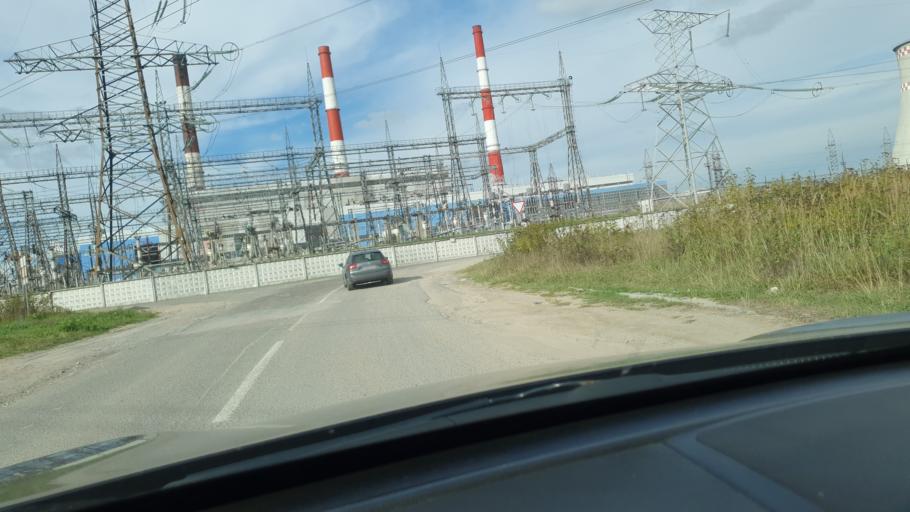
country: BY
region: Minsk
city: Azyartso
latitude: 53.8677
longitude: 27.4001
